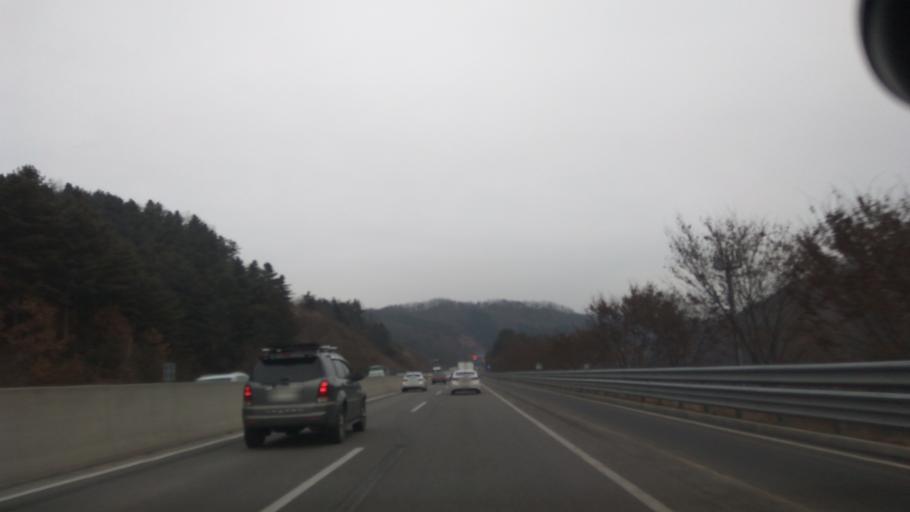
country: KR
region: Gangwon-do
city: Sindong
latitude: 37.7415
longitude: 127.6718
